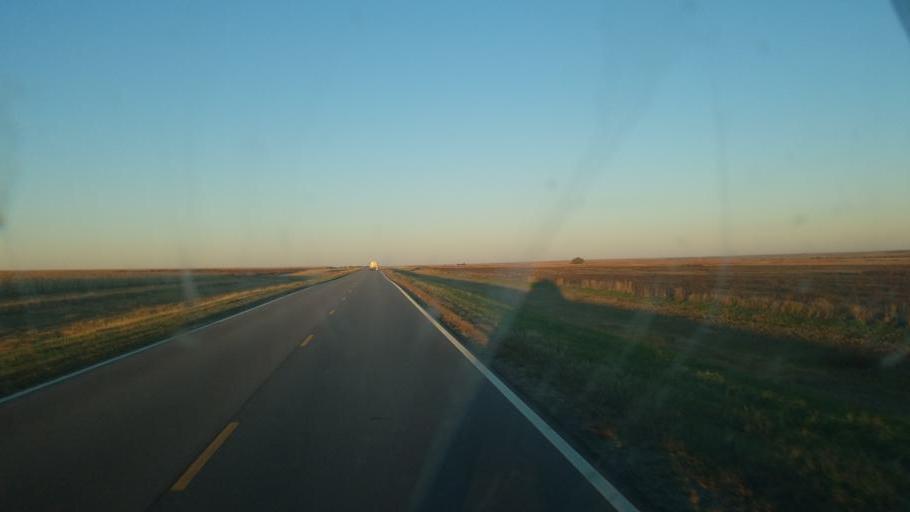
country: US
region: Kansas
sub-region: Wallace County
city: Sharon Springs
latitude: 38.9012
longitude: -101.8459
